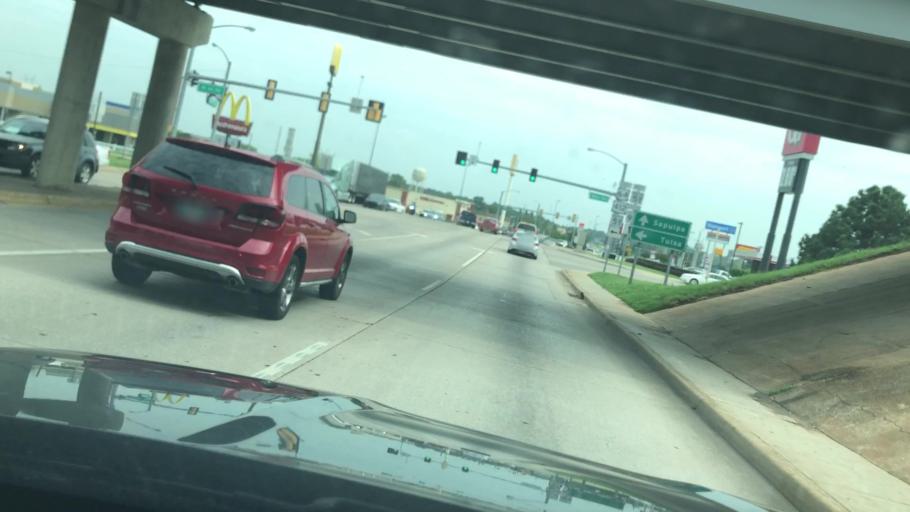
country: US
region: Oklahoma
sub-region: Tulsa County
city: Sand Springs
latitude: 36.1368
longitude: -96.1154
